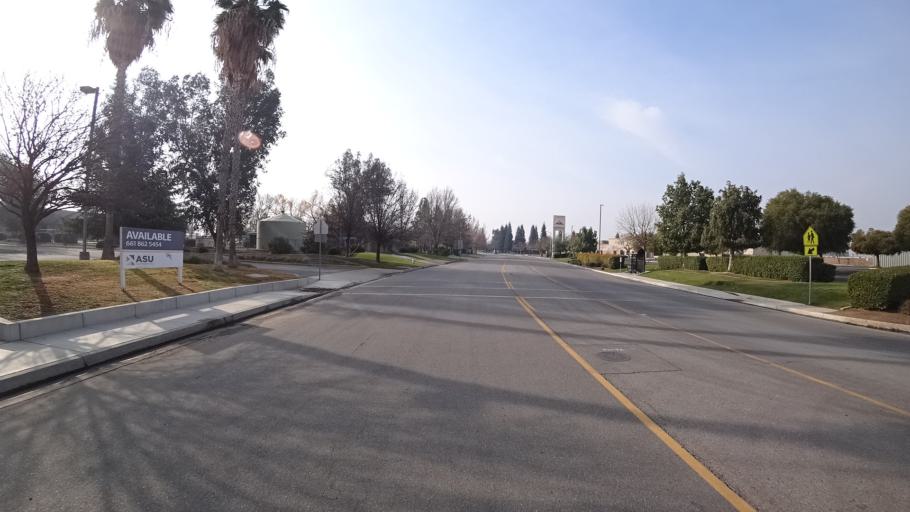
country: US
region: California
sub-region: Kern County
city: Bakersfield
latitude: 35.3919
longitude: -119.0360
